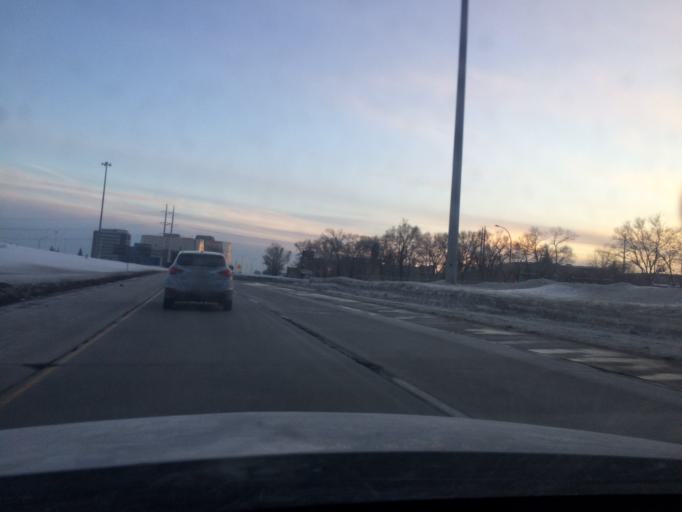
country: CA
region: Quebec
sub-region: Montreal
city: Saint-Leonard
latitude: 45.6044
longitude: -73.5681
